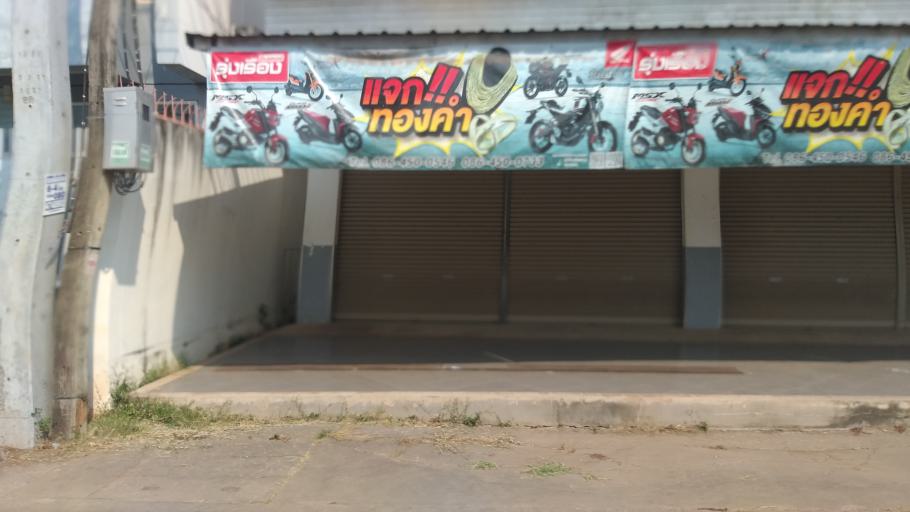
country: TH
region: Changwat Udon Thani
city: Udon Thani
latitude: 17.4197
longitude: 102.7714
